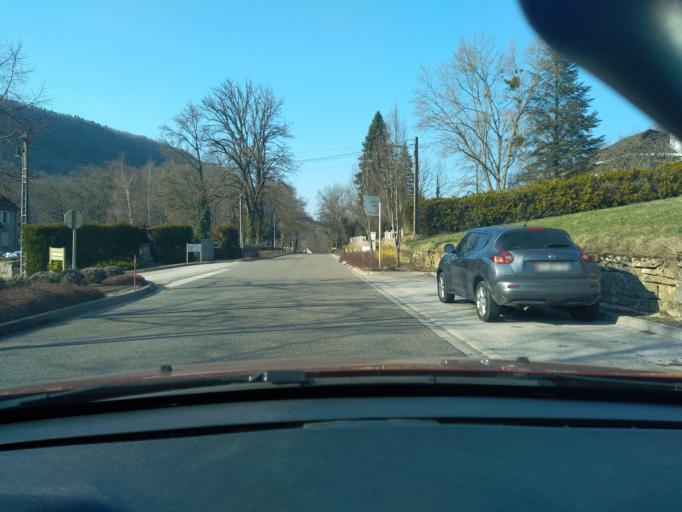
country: FR
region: Franche-Comte
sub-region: Departement du Jura
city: Perrigny
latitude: 46.6370
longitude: 5.6038
